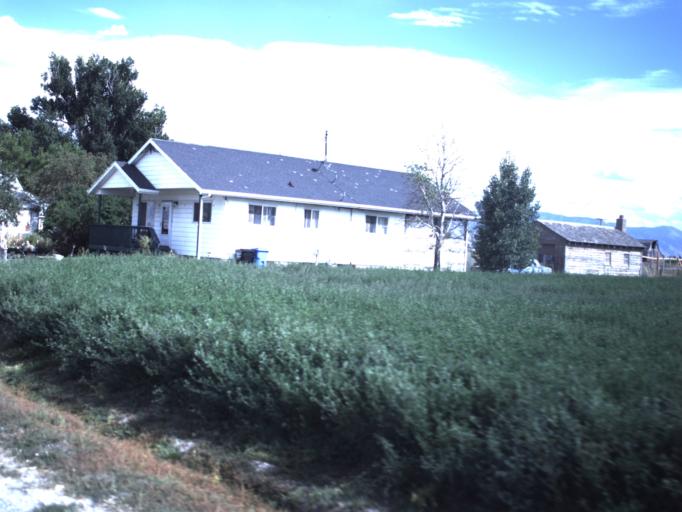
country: US
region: Utah
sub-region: Cache County
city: Lewiston
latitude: 41.9174
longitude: -111.9396
